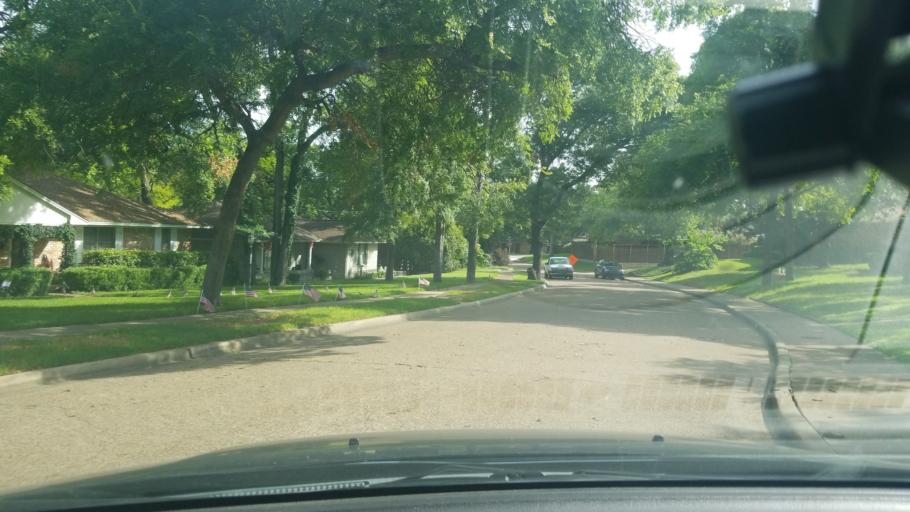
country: US
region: Texas
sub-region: Dallas County
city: Highland Park
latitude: 32.7983
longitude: -96.7032
